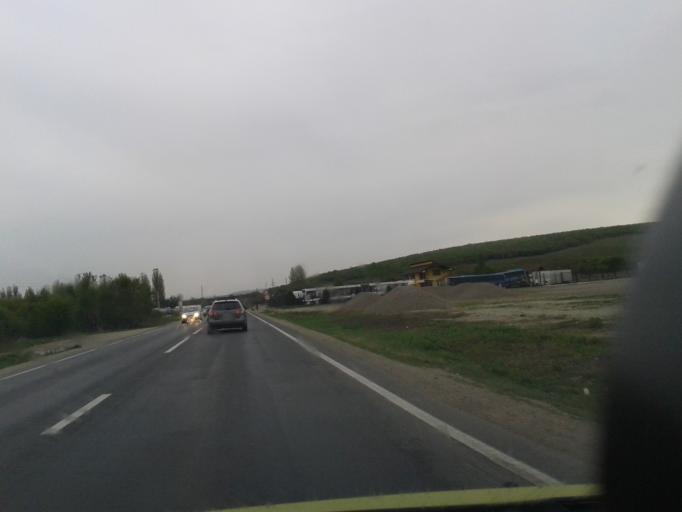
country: RO
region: Hunedoara
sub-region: Municipiul Deva
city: Cristur
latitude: 45.8518
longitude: 22.9720
